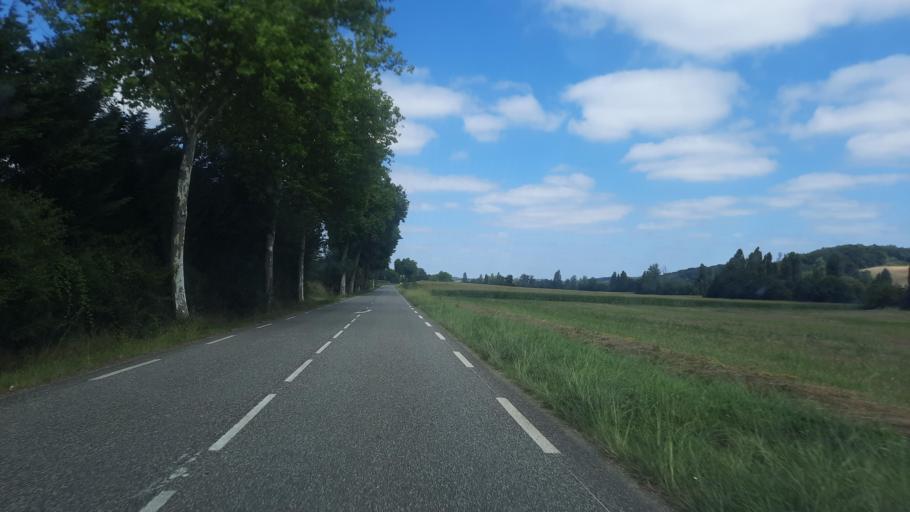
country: FR
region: Midi-Pyrenees
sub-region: Departement de la Haute-Garonne
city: Boulogne-sur-Gesse
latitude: 43.3861
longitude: 0.7749
